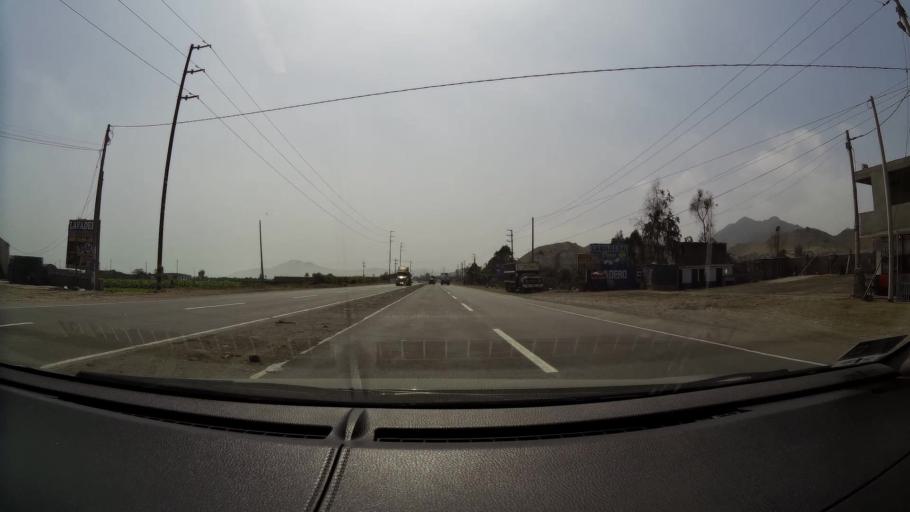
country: PE
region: Lima
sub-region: Provincia de Huaral
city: Chancay
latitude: -11.5286
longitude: -77.2876
